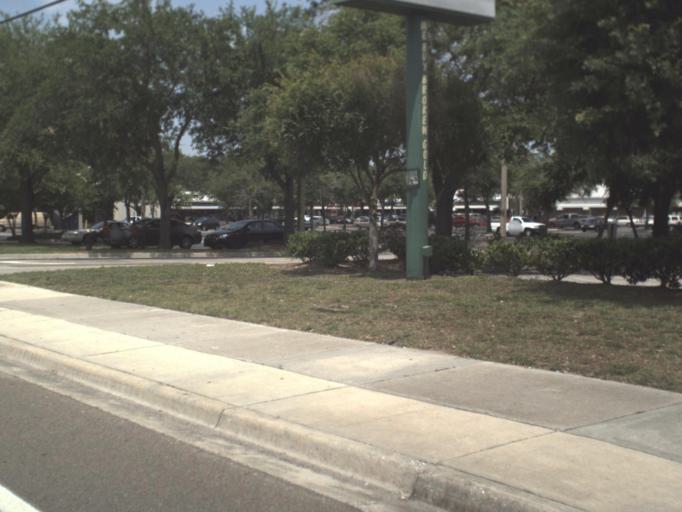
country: US
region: Florida
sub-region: Duval County
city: Jacksonville
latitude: 30.3742
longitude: -81.6512
